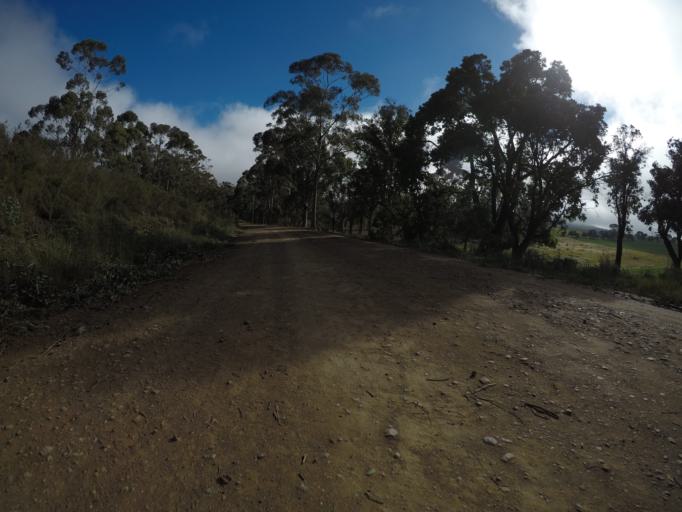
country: ZA
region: Western Cape
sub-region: Cape Winelands District Municipality
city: Ashton
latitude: -34.1130
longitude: 19.8027
